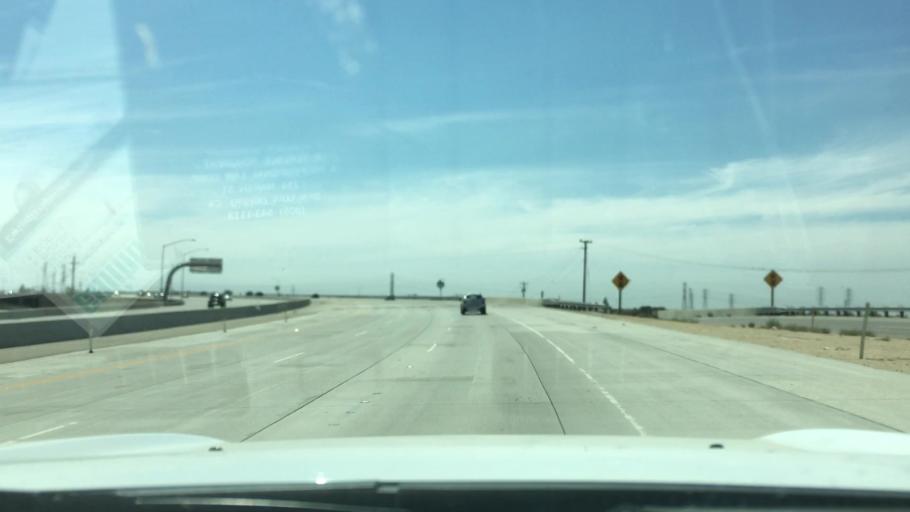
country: US
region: California
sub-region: Kern County
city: Greenacres
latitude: 35.3686
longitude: -119.0861
